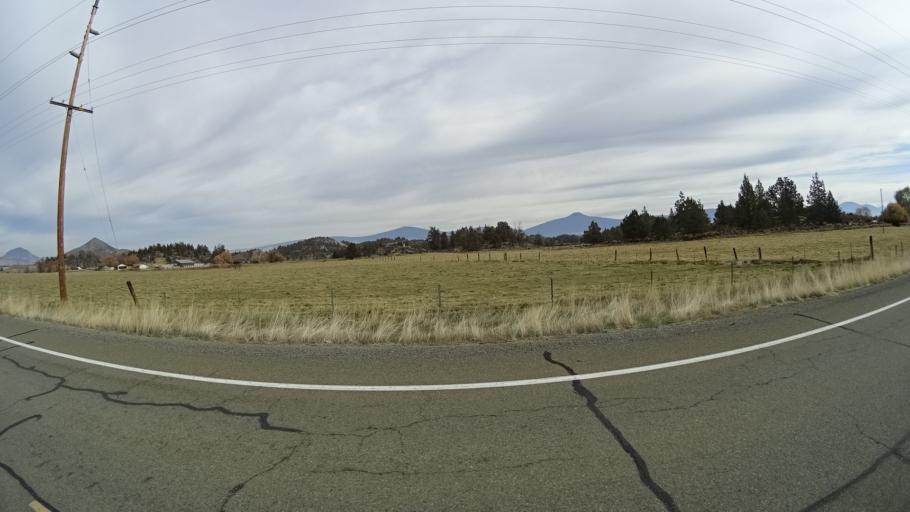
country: US
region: California
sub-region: Siskiyou County
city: Montague
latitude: 41.6791
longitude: -122.5284
